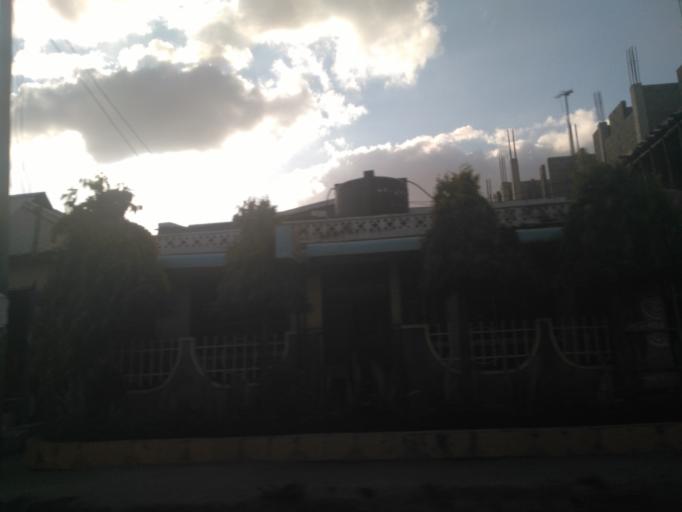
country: TZ
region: Dar es Salaam
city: Dar es Salaam
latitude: -6.8512
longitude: 39.2579
